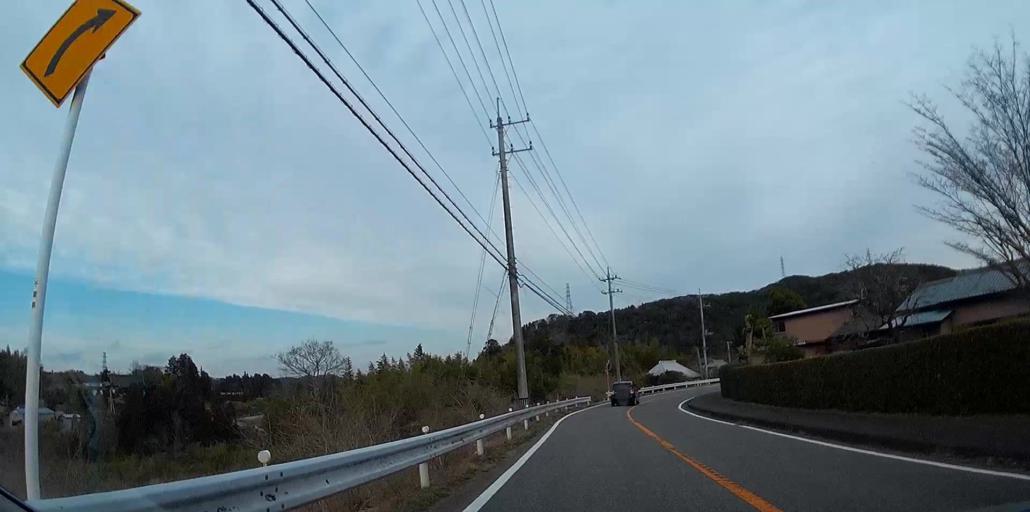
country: JP
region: Chiba
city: Kisarazu
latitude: 35.2681
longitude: 140.0582
